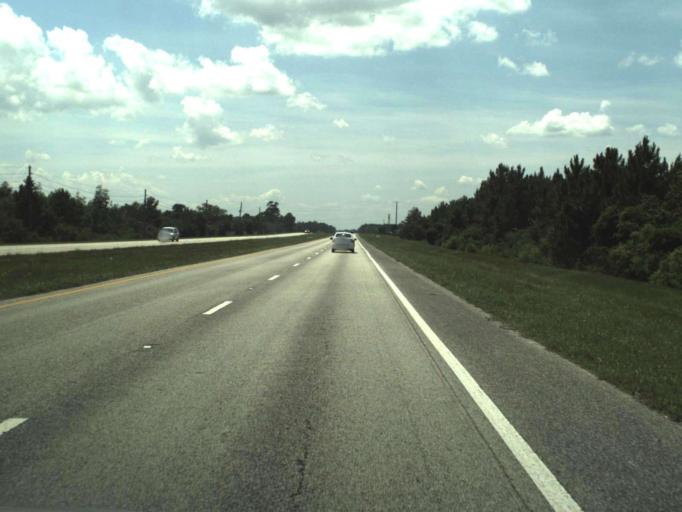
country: US
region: Florida
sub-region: Volusia County
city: Samsula-Spruce Creek
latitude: 29.0150
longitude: -81.0927
